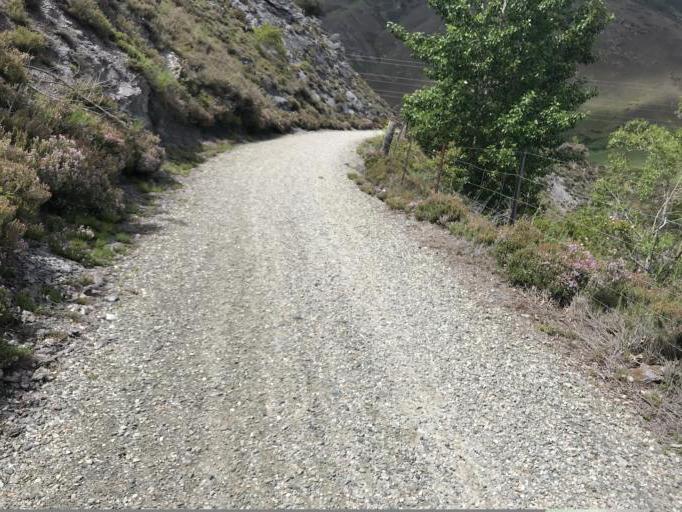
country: NZ
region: Otago
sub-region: Queenstown-Lakes District
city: Arrowtown
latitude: -45.0054
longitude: 168.8813
